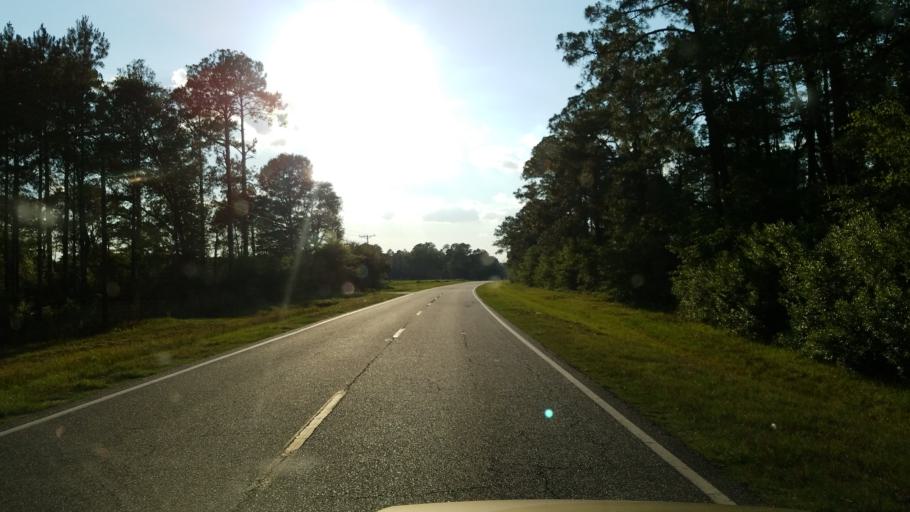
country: US
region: Georgia
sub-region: Berrien County
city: Nashville
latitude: 31.1914
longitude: -83.2073
